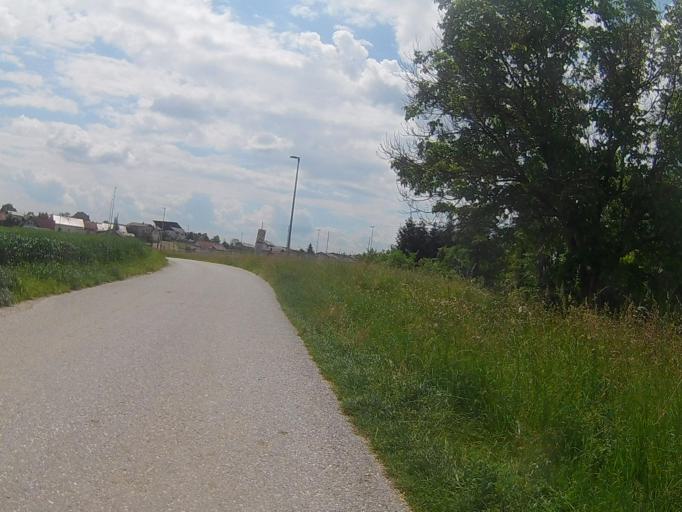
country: SI
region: Starse
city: Starse
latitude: 46.4592
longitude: 15.7897
